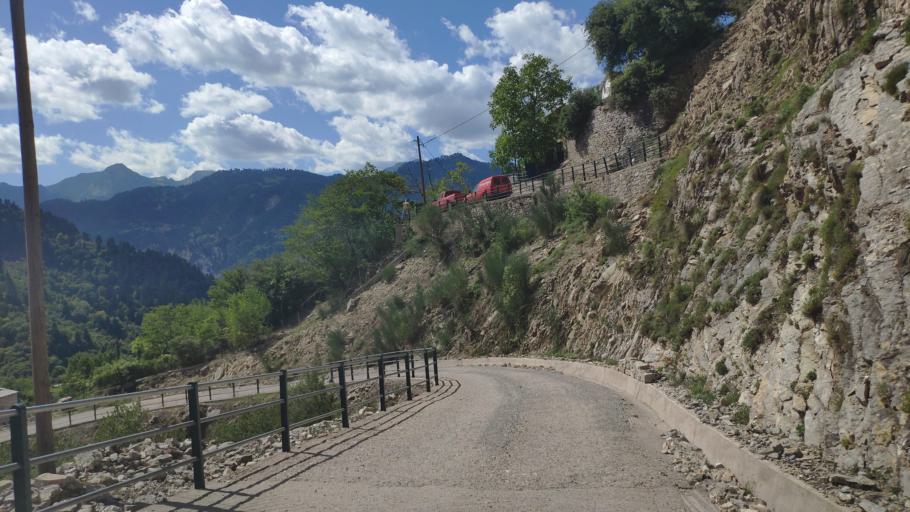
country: GR
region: Central Greece
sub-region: Nomos Evrytanias
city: Kerasochori
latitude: 39.1368
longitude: 21.6515
